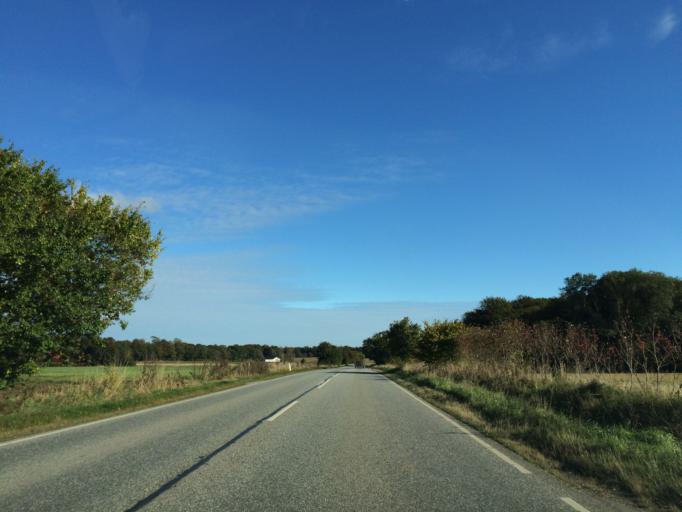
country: DK
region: Central Jutland
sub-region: Randers Kommune
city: Langa
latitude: 56.3911
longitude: 9.9701
